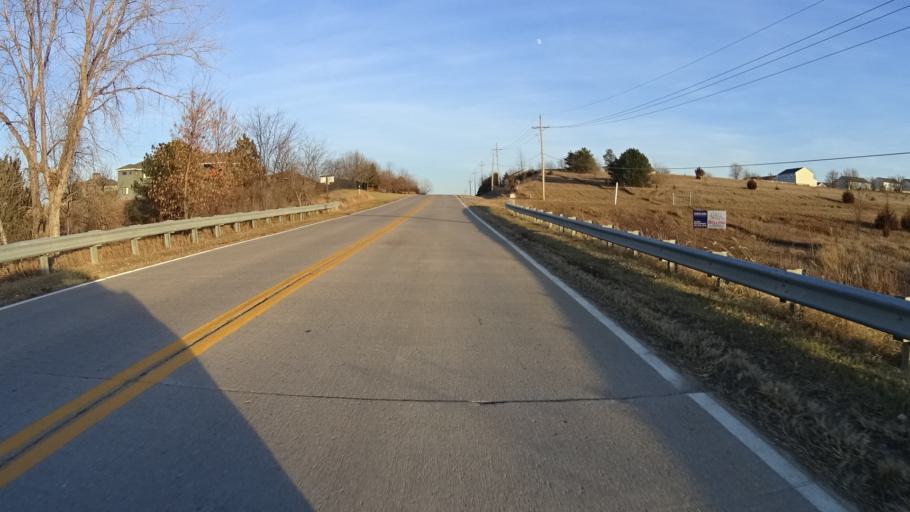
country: US
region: Nebraska
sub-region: Sarpy County
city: Papillion
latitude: 41.1326
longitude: -96.0742
